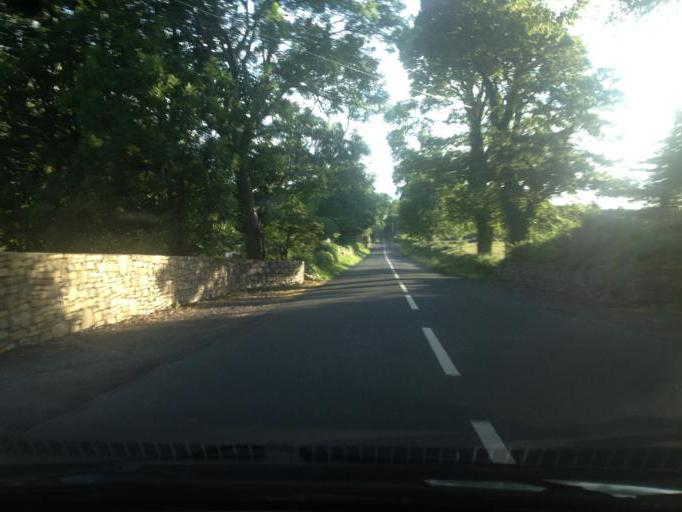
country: IE
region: Connaught
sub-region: Sligo
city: Sligo
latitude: 54.2822
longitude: -8.4200
